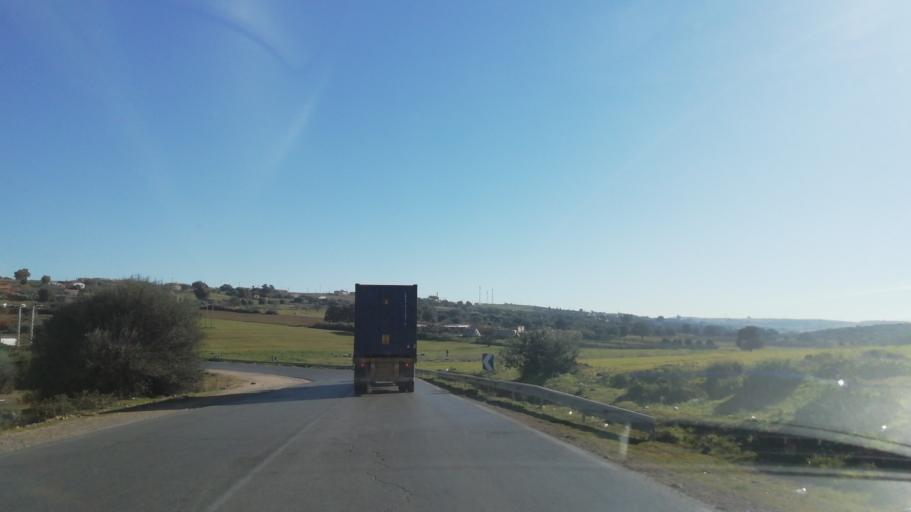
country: DZ
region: Relizane
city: Smala
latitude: 35.6856
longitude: 0.7967
